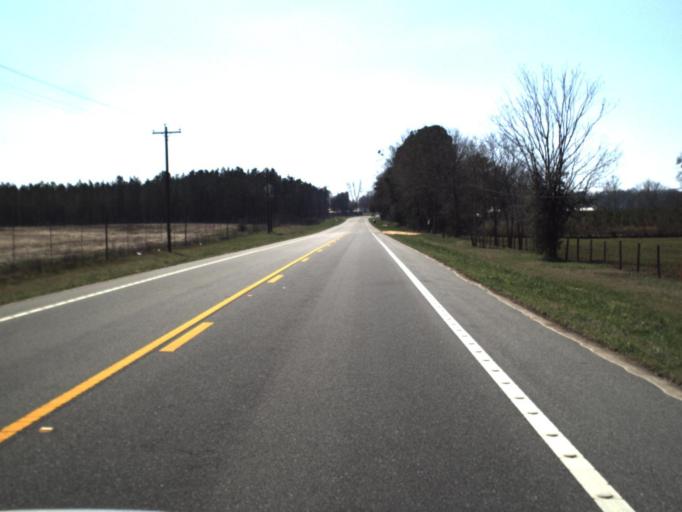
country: US
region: Florida
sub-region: Jackson County
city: Sneads
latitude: 30.6914
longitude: -85.0219
